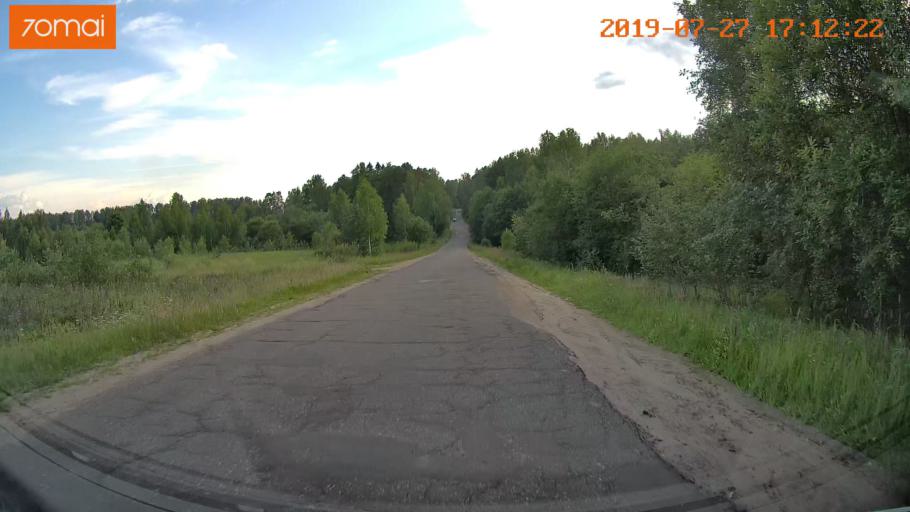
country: RU
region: Ivanovo
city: Novo-Talitsy
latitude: 57.0590
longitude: 40.8619
